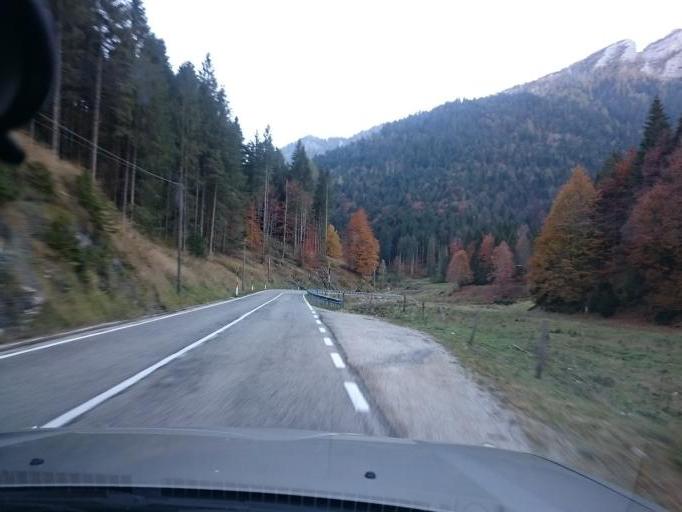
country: IT
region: Veneto
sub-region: Provincia di Vicenza
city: Roana
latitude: 45.9440
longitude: 11.4363
